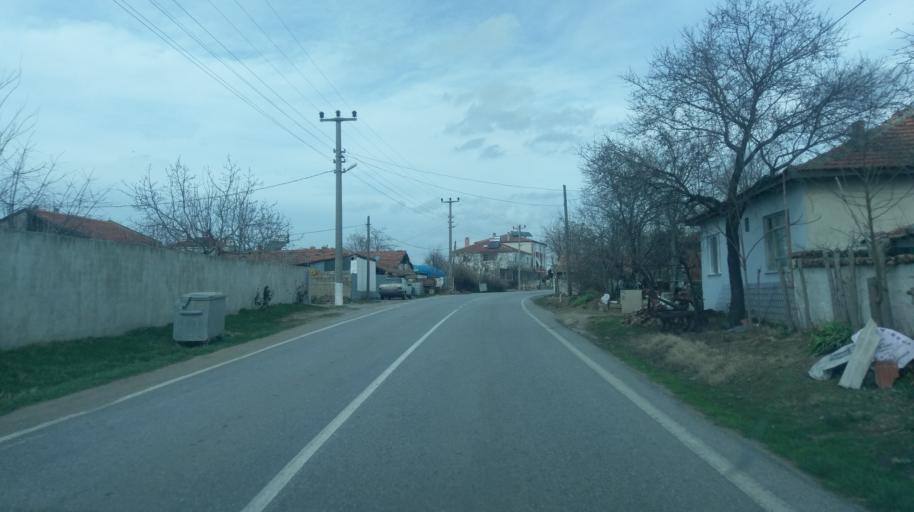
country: TR
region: Edirne
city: Havsa
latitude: 41.5830
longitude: 26.8359
